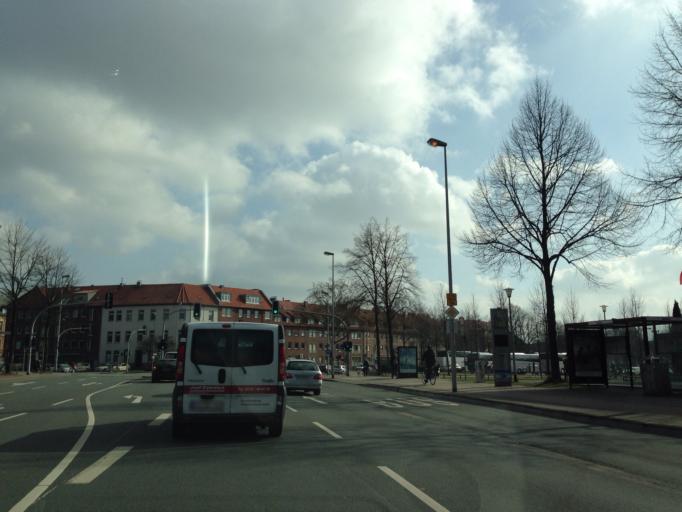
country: DE
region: North Rhine-Westphalia
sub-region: Regierungsbezirk Munster
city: Muenster
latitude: 51.9669
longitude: 7.6158
